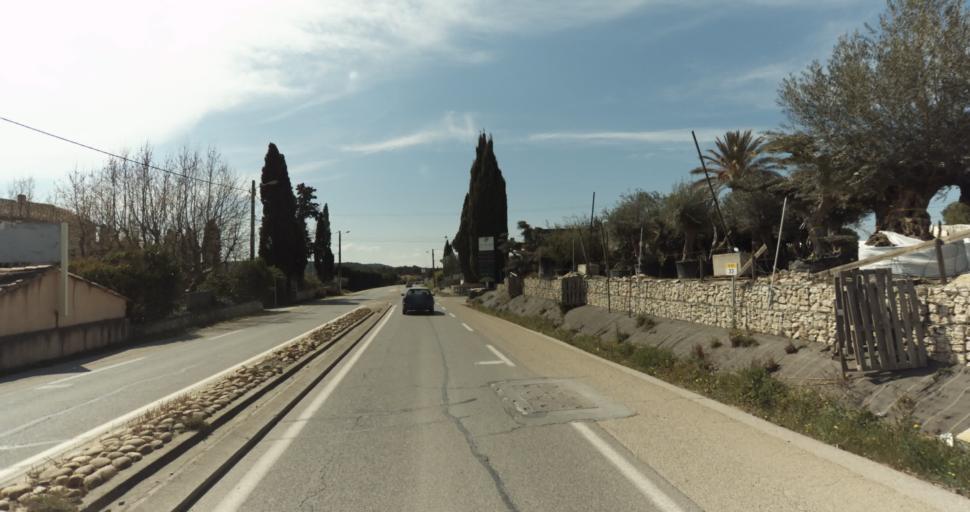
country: FR
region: Provence-Alpes-Cote d'Azur
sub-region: Departement des Bouches-du-Rhone
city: Ventabren
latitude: 43.5440
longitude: 5.2769
